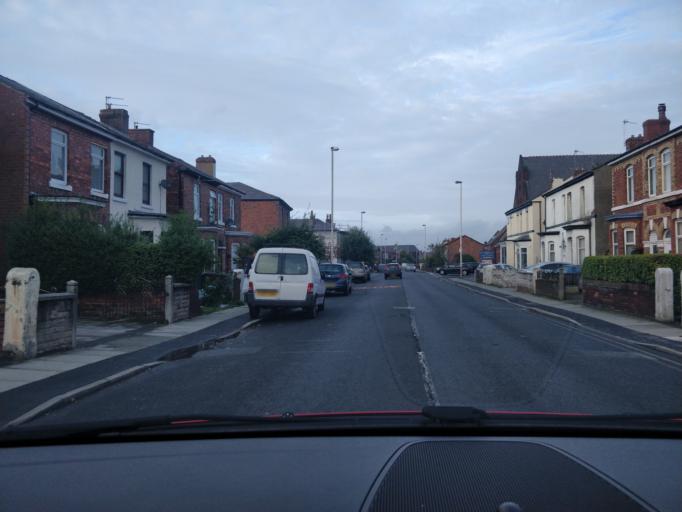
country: GB
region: England
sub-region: Sefton
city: Southport
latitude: 53.6462
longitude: -2.9866
